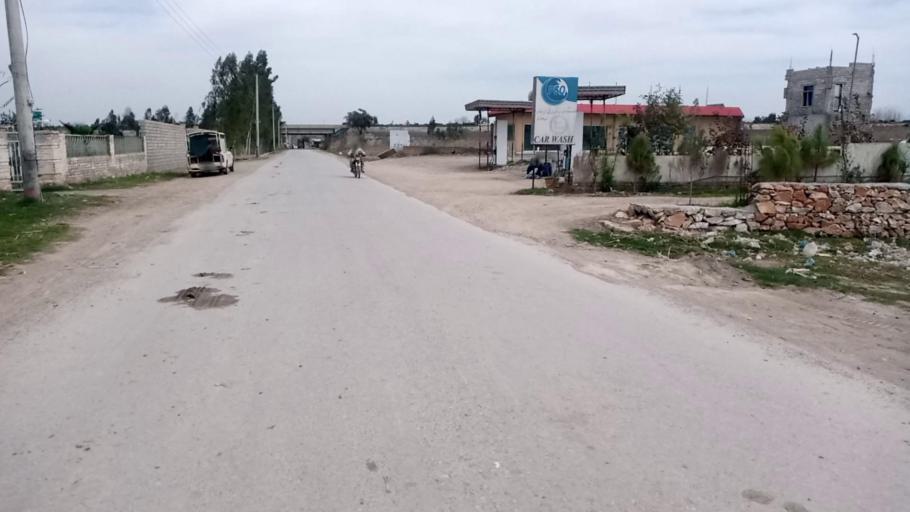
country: PK
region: Khyber Pakhtunkhwa
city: Charsadda
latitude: 34.0620
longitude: 71.7034
